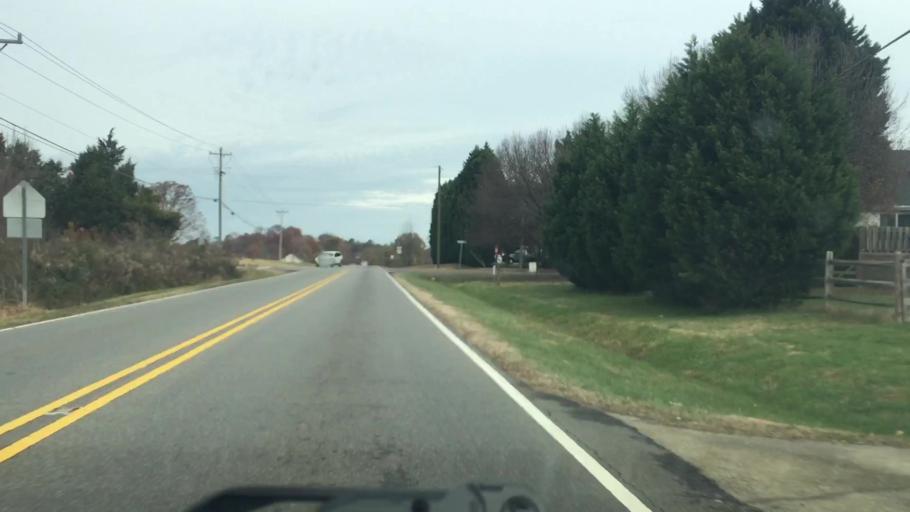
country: US
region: North Carolina
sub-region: Iredell County
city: Mooresville
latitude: 35.6004
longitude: -80.8389
